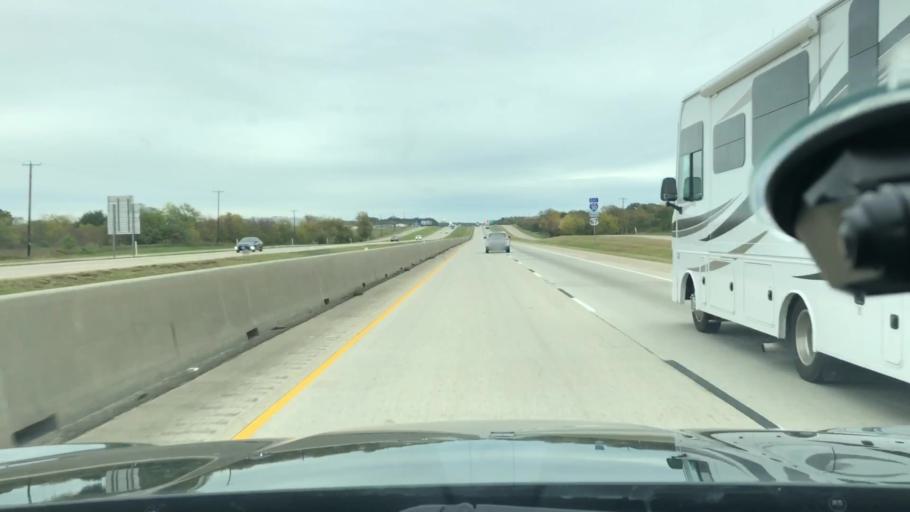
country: US
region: Texas
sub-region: Hopkins County
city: Sulphur Springs
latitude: 33.1211
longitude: -95.6645
